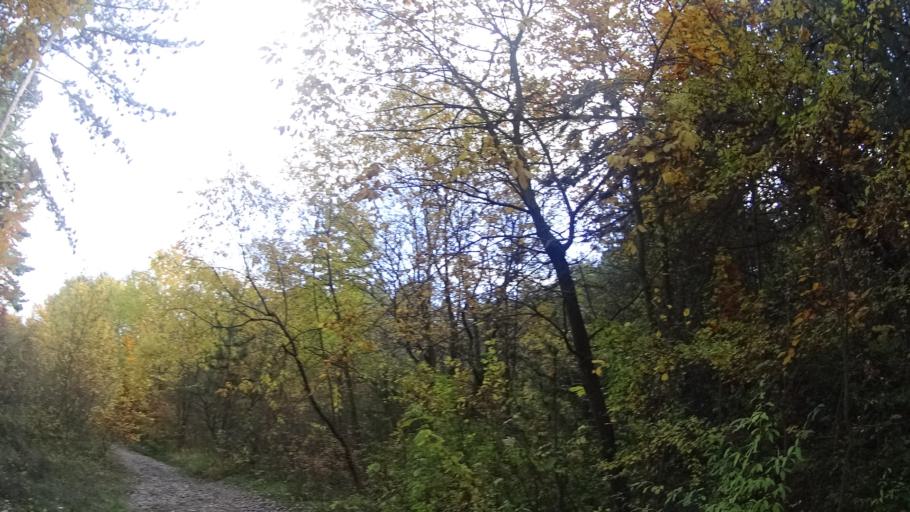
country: DE
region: Thuringia
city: Arnstadt
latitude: 50.8337
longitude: 10.9210
